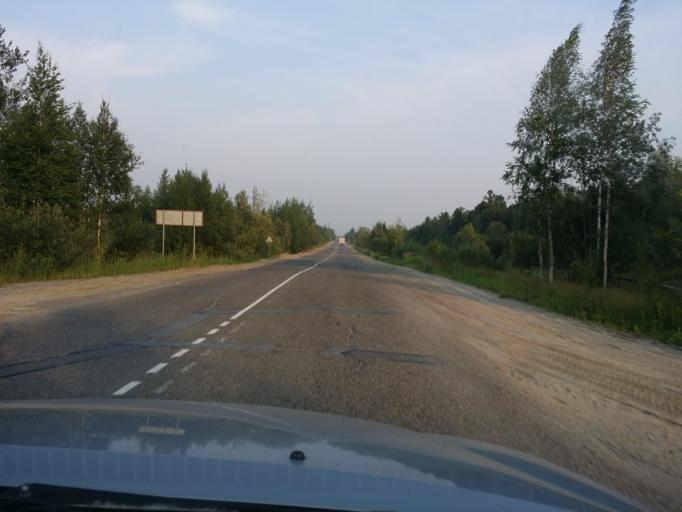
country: RU
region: Khanty-Mansiyskiy Avtonomnyy Okrug
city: Nizhnevartovsk
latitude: 61.2014
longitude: 76.5378
